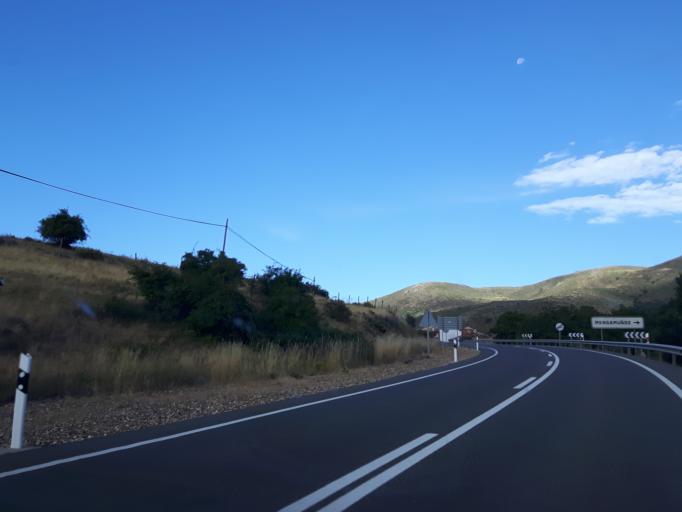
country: ES
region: Castille and Leon
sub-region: Provincia de Avila
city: Mengamunoz
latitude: 40.5021
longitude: -4.9962
